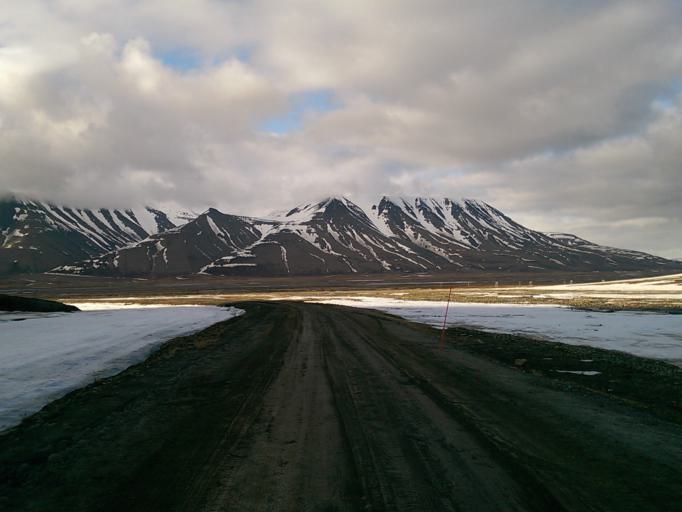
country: SJ
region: Svalbard
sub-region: Spitsbergen
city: Longyearbyen
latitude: 78.1881
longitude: 15.7804
